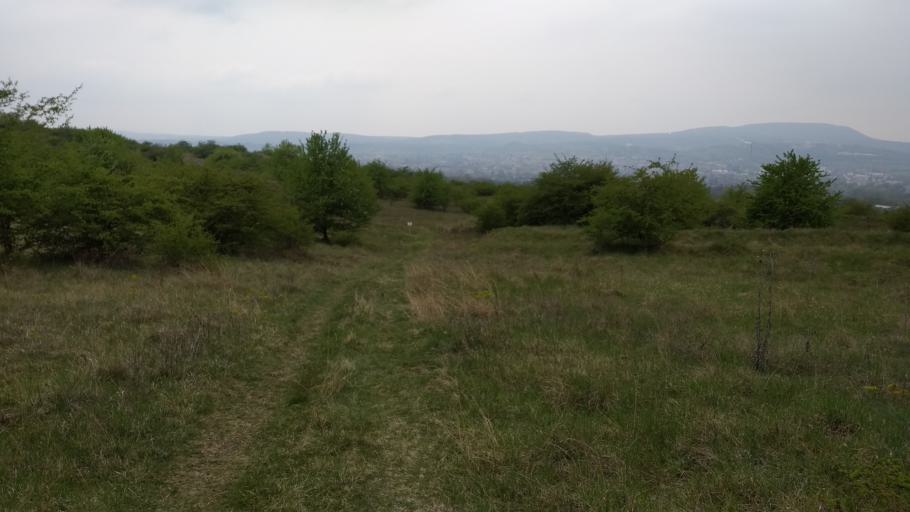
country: HU
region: Komarom-Esztergom
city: Dorog
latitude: 47.7401
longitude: 18.7595
